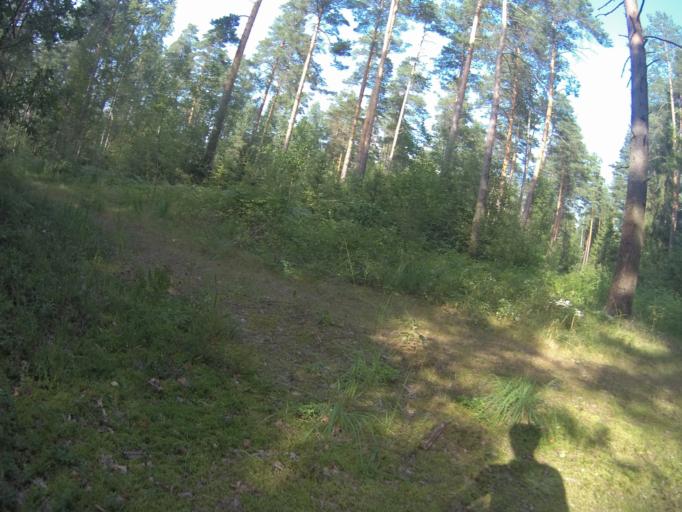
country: RU
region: Vladimir
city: Kommunar
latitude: 56.0817
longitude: 40.5058
